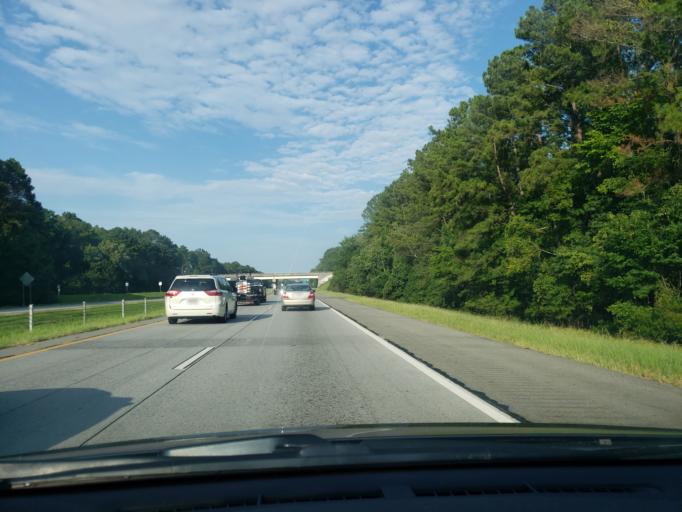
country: US
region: Georgia
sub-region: Chatham County
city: Garden City
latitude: 32.0697
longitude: -81.1637
